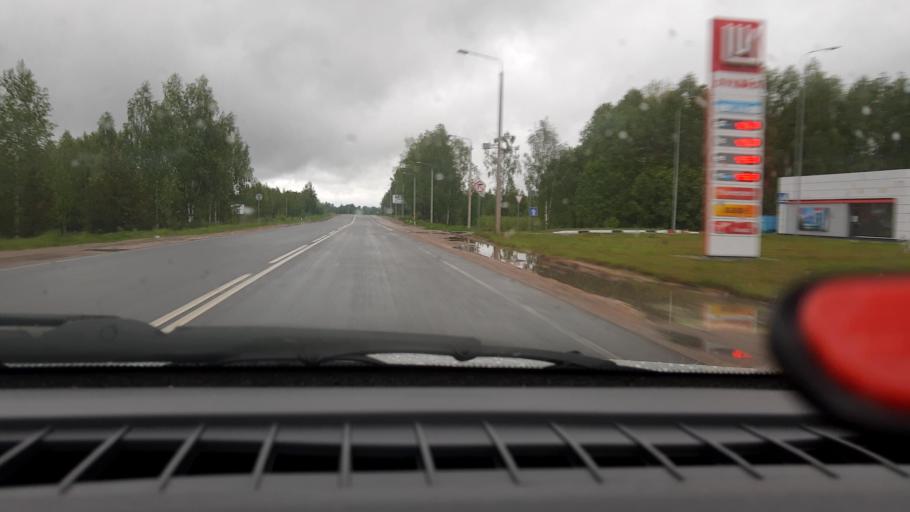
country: RU
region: Nizjnij Novgorod
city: Semenov
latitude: 56.8223
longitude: 44.5814
